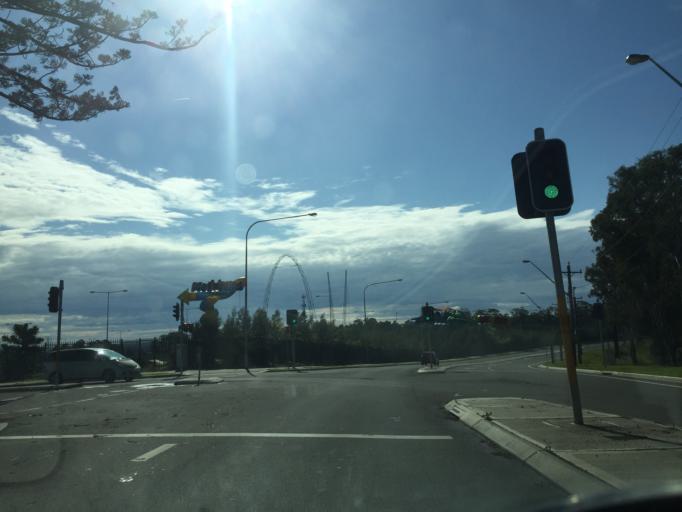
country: AU
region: New South Wales
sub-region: Holroyd
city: Girraween
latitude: -33.8083
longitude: 150.9074
